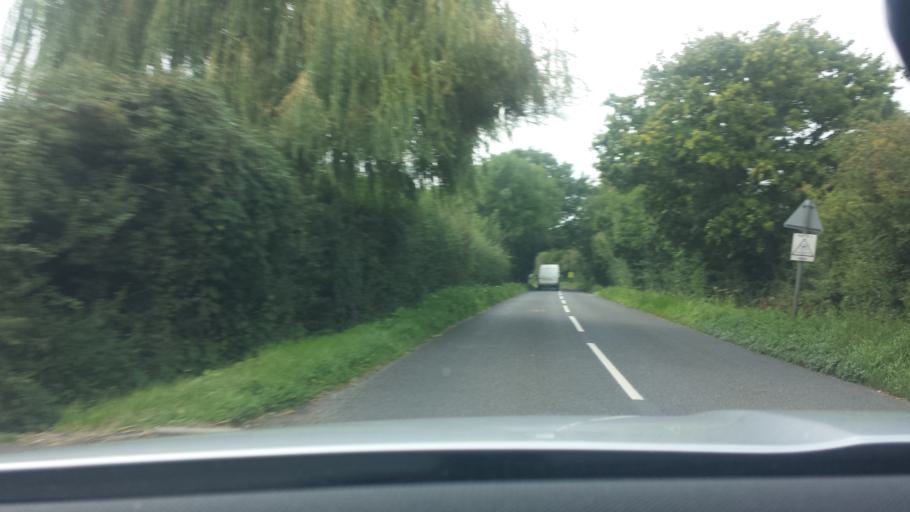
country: GB
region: England
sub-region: Kent
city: Marden
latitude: 51.1862
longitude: 0.4669
